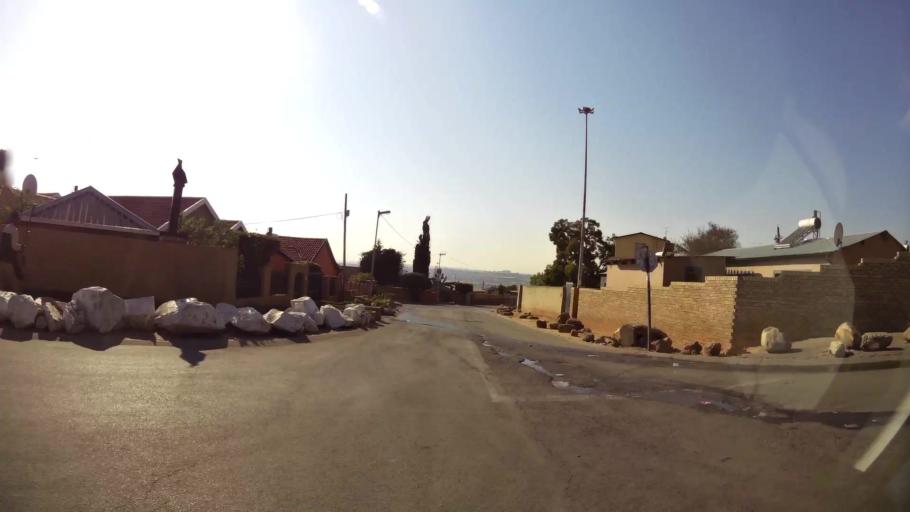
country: ZA
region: Gauteng
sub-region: City of Johannesburg Metropolitan Municipality
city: Modderfontein
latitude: -26.1093
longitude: 28.0916
